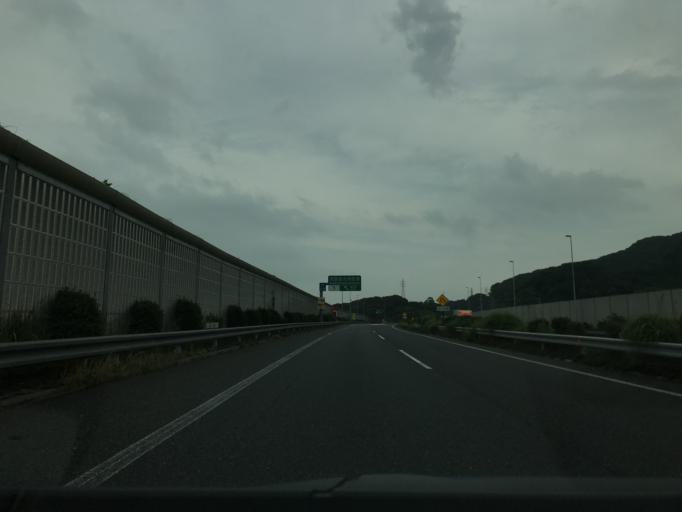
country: JP
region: Fukuoka
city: Kanda
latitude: 33.7973
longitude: 130.9632
